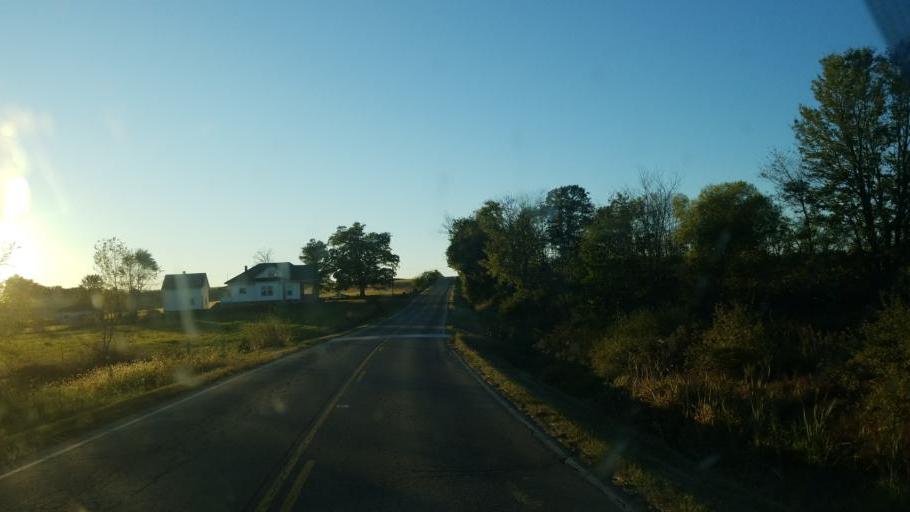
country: US
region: Ohio
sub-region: Knox County
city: Oak Hill
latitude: 40.3335
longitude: -82.1845
